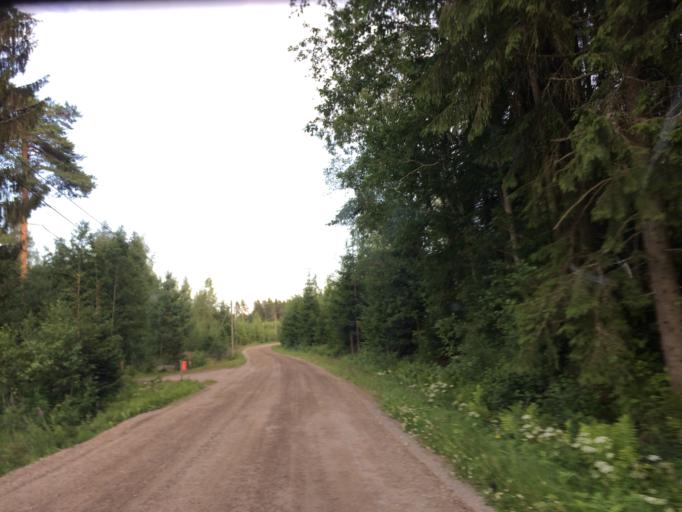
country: FI
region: Haeme
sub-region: Haemeenlinna
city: Janakkala
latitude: 60.8879
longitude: 24.6077
